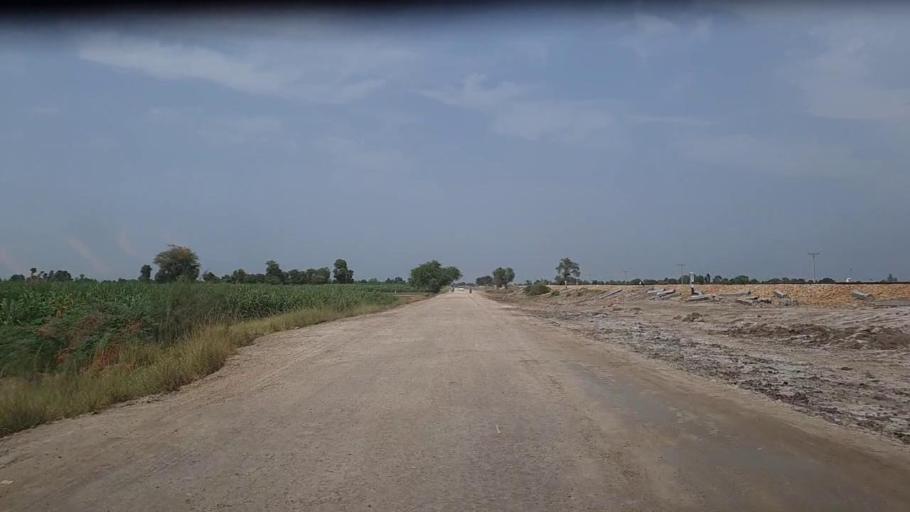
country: PK
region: Sindh
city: Bhiria
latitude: 26.9044
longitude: 68.2903
